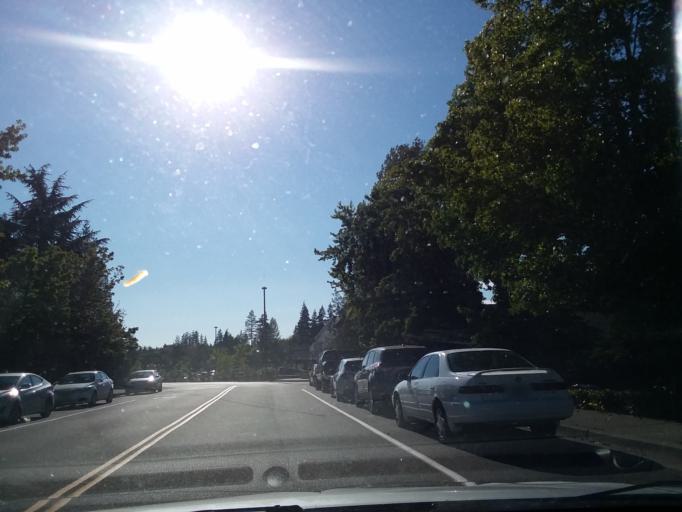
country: US
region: Washington
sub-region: Snohomish County
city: Alderwood Manor
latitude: 47.8339
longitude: -122.2703
